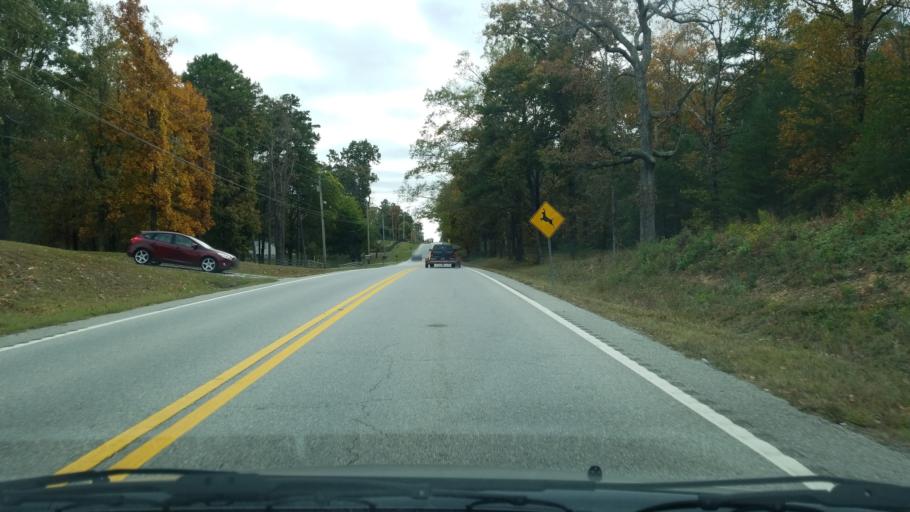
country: US
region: Tennessee
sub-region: Hamilton County
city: Lakesite
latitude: 35.2235
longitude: -85.0245
